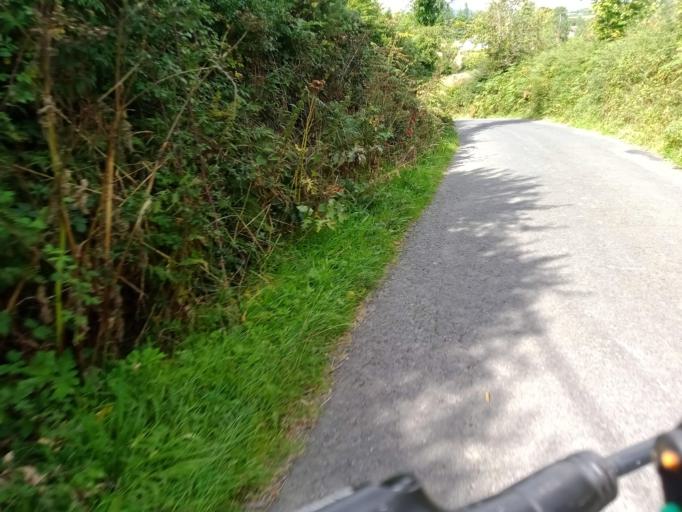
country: IE
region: Munster
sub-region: Waterford
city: Dungarvan
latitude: 52.1382
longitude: -7.4790
